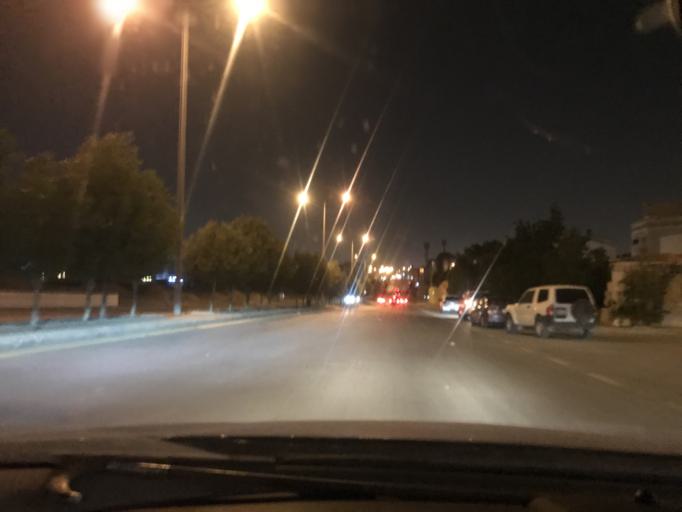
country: SA
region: Ar Riyad
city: Riyadh
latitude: 24.7537
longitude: 46.7546
